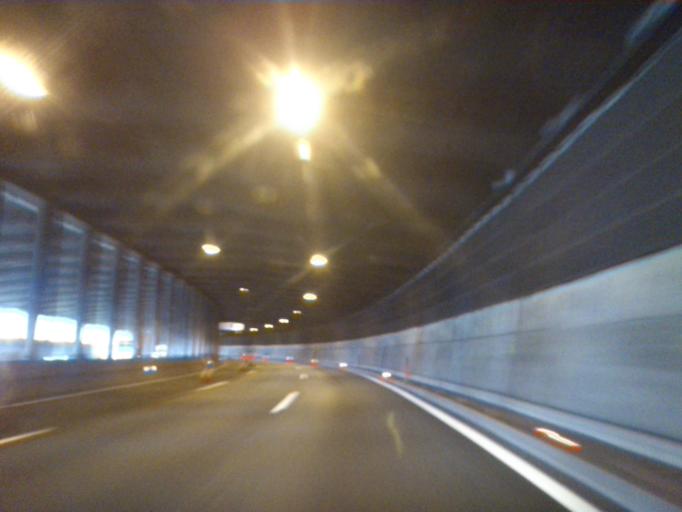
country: AT
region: Tyrol
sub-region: Politischer Bezirk Innsbruck Land
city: Schoenberg im Stubaital
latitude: 47.1856
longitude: 11.4010
